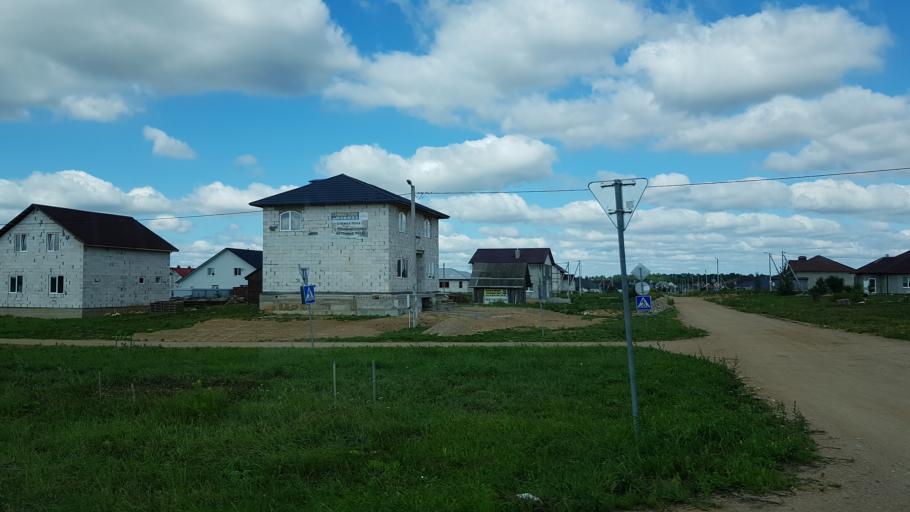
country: BY
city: Fanipol
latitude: 53.7293
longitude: 27.3313
